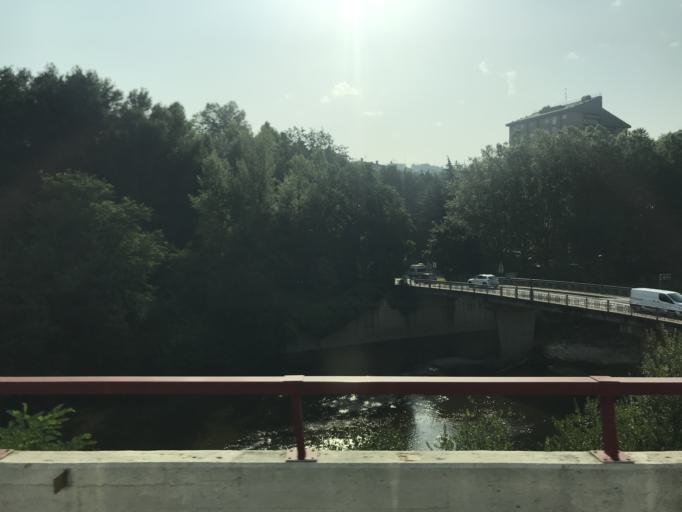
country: ES
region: Basque Country
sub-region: Provincia de Guipuzcoa
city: Andoain
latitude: 43.2194
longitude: -2.0247
